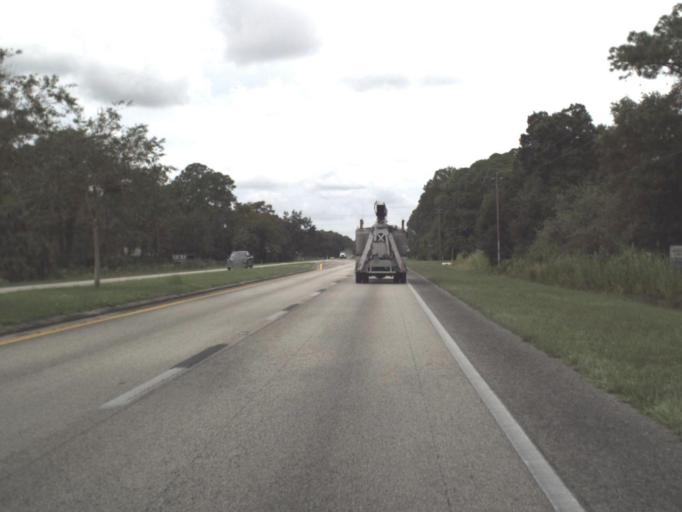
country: US
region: Florida
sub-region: Lee County
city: Olga
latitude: 26.7145
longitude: -81.6984
